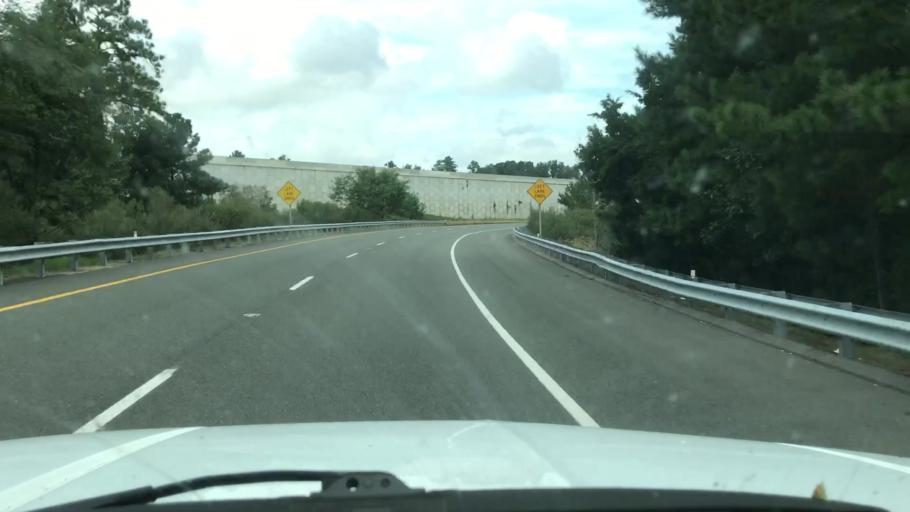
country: US
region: Virginia
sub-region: Henrico County
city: Short Pump
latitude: 37.6566
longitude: -77.6021
